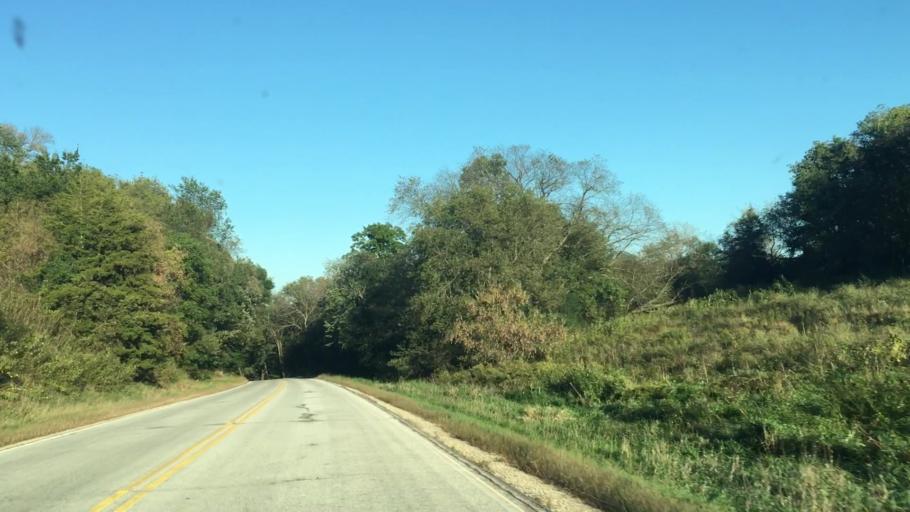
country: US
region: Minnesota
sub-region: Fillmore County
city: Chatfield
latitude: 43.8173
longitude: -92.0580
